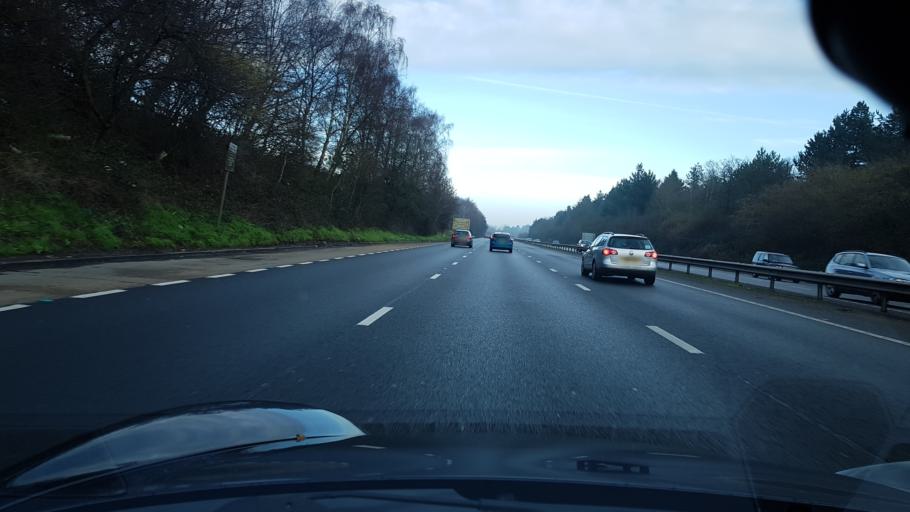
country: GB
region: England
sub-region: Surrey
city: Ripley
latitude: 51.2991
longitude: -0.4839
